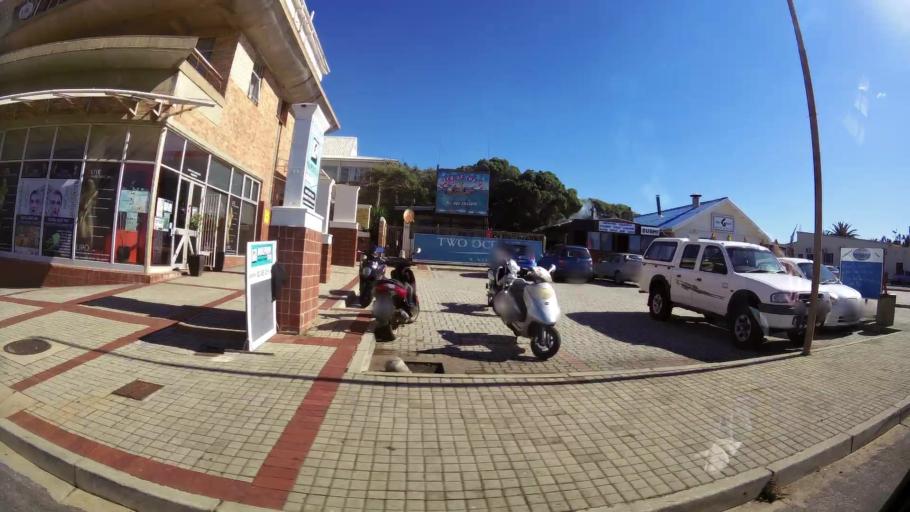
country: ZA
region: Eastern Cape
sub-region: Cacadu District Municipality
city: Jeffrey's Bay
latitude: -34.0524
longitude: 24.9236
